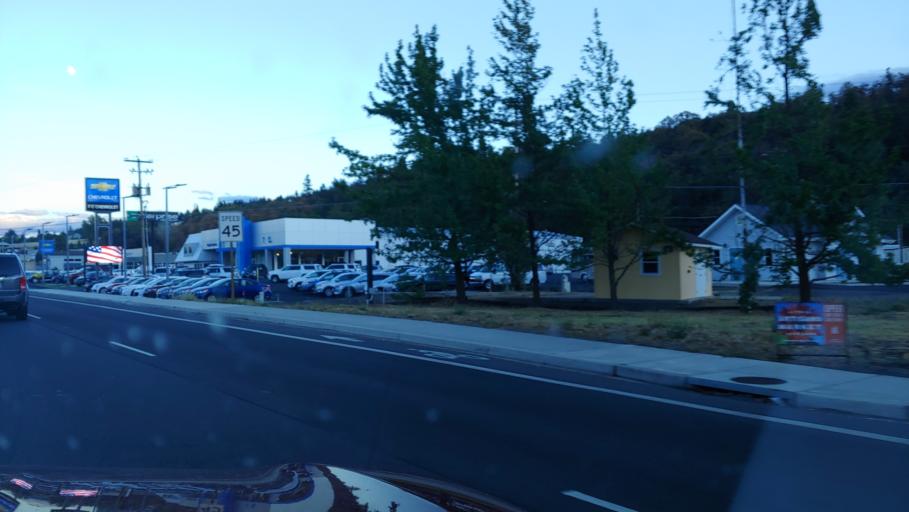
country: US
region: Oregon
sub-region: Jackson County
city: Ashland
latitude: 42.2207
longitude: -122.7405
